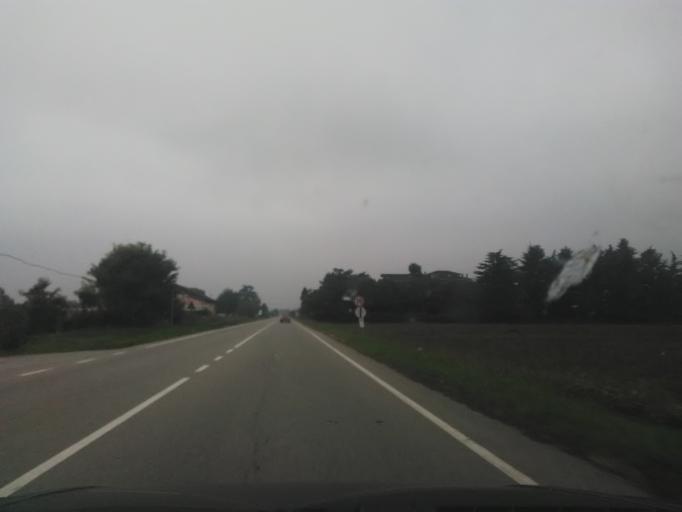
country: IT
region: Piedmont
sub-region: Provincia di Vercelli
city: Santhia
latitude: 45.3733
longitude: 8.1668
